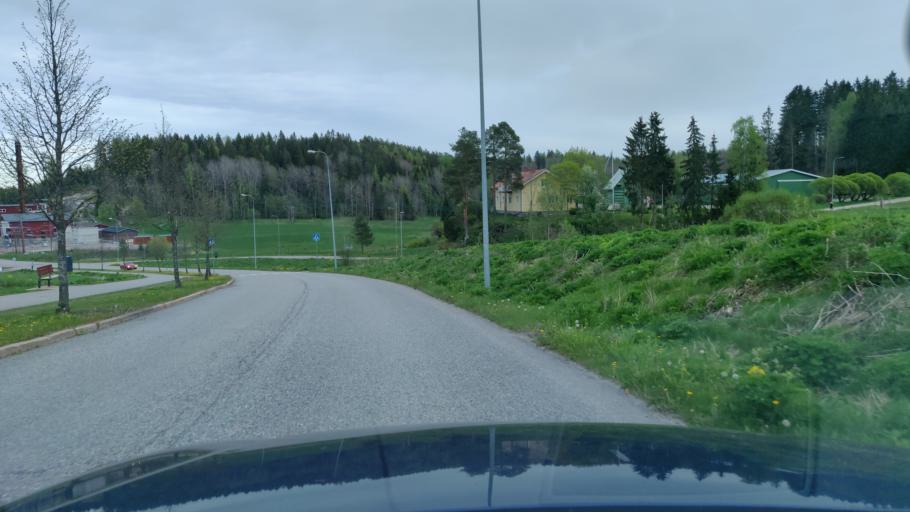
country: FI
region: Uusimaa
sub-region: Helsinki
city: Nurmijaervi
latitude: 60.3848
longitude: 24.7595
